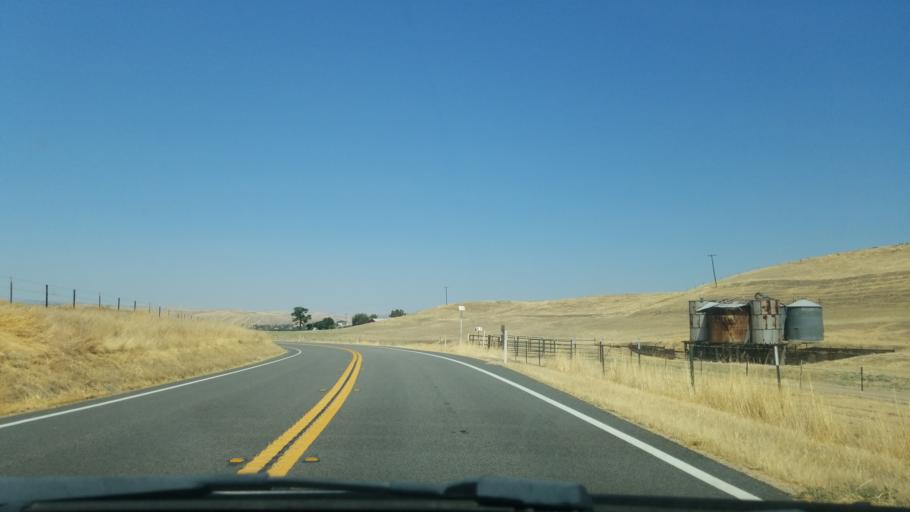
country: US
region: California
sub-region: San Luis Obispo County
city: Shandon
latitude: 35.6190
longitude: -120.4004
